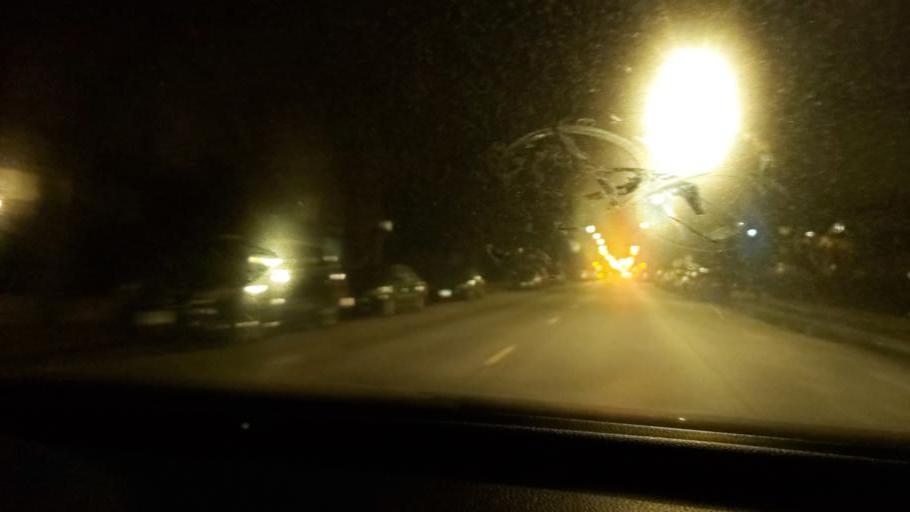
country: US
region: Illinois
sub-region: Cook County
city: Lincolnwood
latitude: 41.9829
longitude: -87.7172
